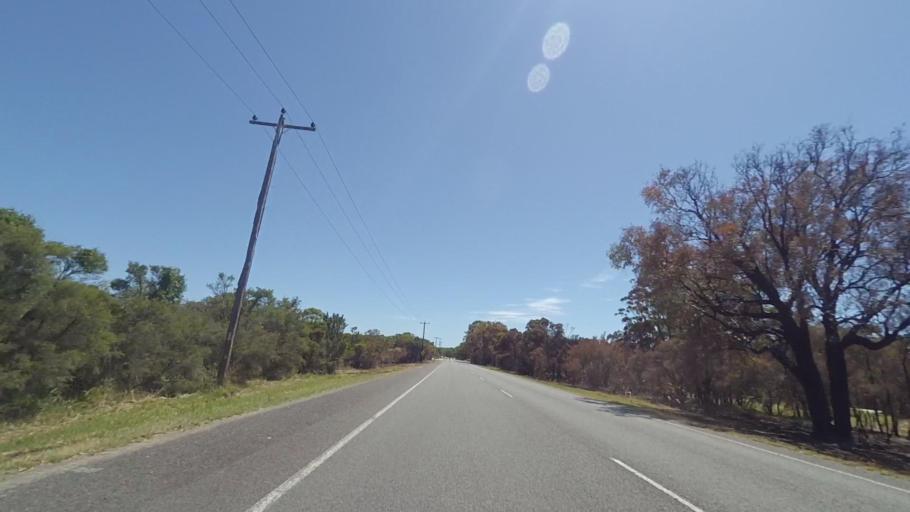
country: AU
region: New South Wales
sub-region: Port Stephens Shire
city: Medowie
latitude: -32.7861
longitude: 151.8564
